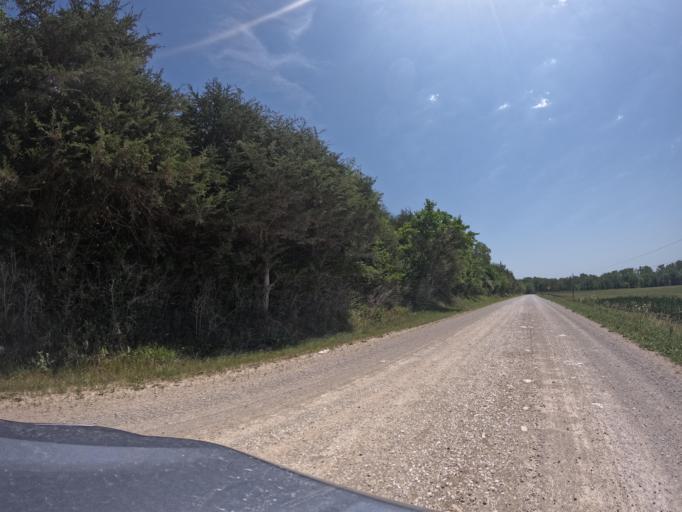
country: US
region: Iowa
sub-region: Henry County
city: Mount Pleasant
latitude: 40.8891
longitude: -91.5401
